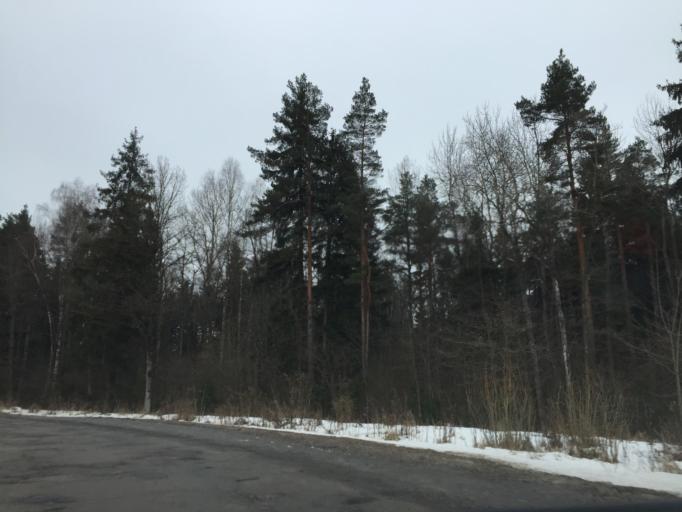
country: LV
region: Ozolnieku
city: Ozolnieki
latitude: 56.6340
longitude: 23.7704
